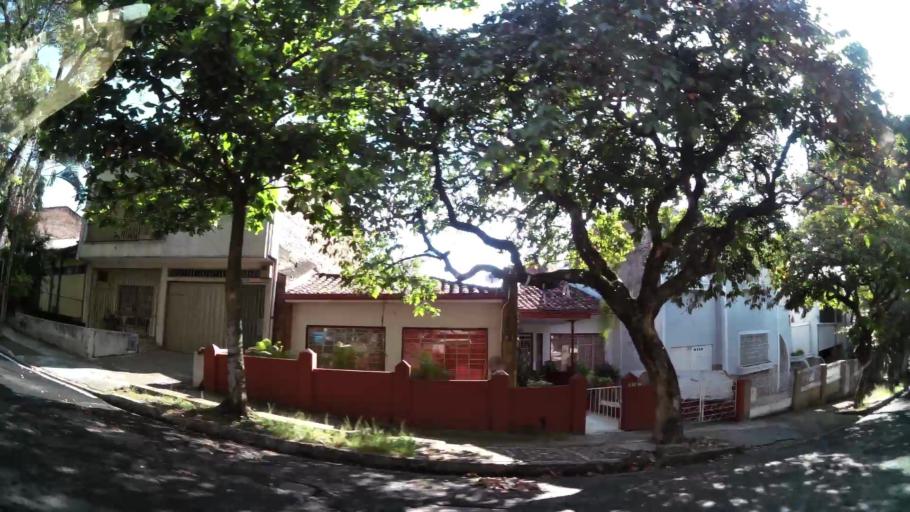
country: CO
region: Valle del Cauca
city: Cali
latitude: 3.4384
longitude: -76.5406
